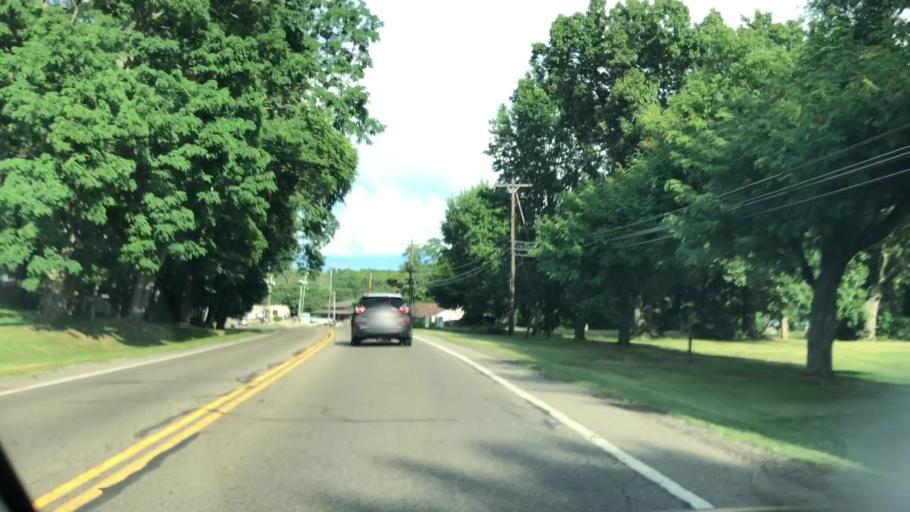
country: US
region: Ohio
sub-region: Summit County
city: Portage Lakes
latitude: 40.9773
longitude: -81.5265
